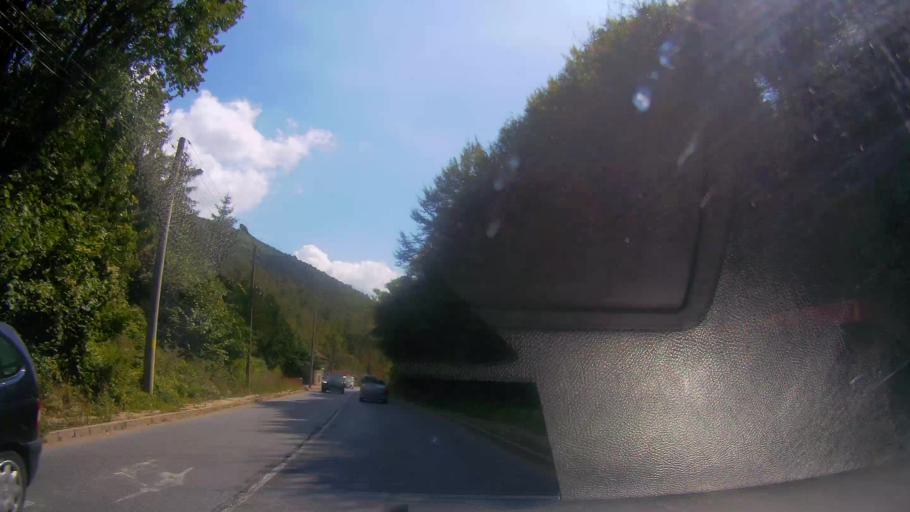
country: BG
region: Stara Zagora
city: Gurkovo
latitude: 42.7186
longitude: 25.7156
